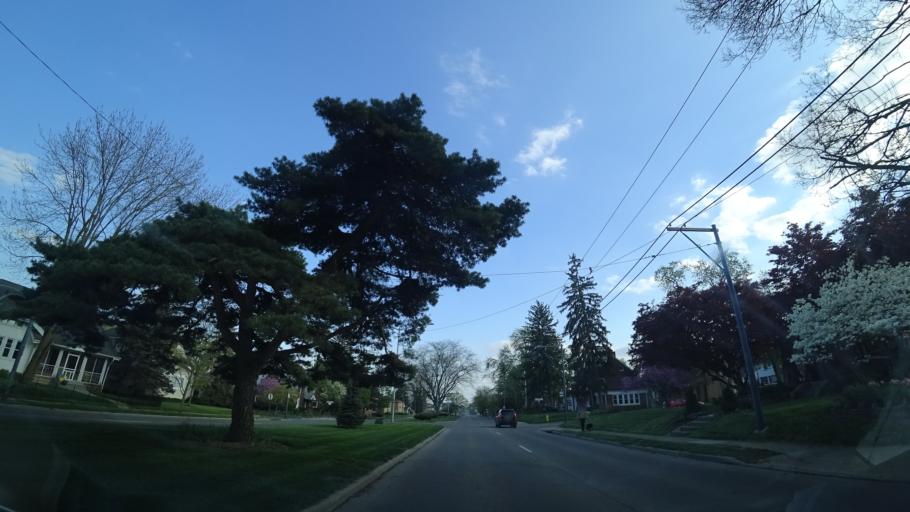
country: US
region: Ohio
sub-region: Montgomery County
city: Oakwood
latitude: 39.7130
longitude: -84.1717
